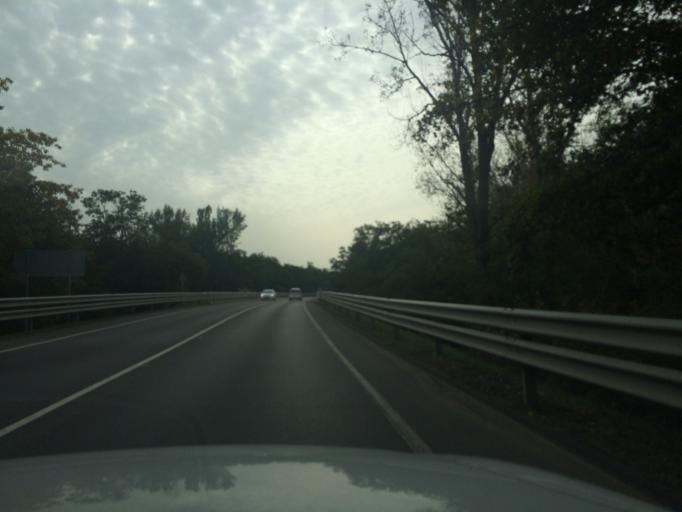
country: HU
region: Szabolcs-Szatmar-Bereg
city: Nyiregyhaza
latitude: 47.9943
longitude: 21.7244
